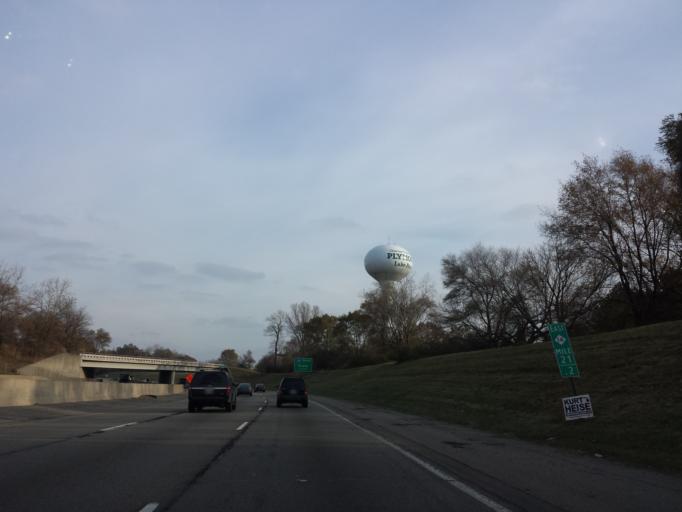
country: US
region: Michigan
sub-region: Wayne County
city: Plymouth
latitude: 42.3876
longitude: -83.4515
